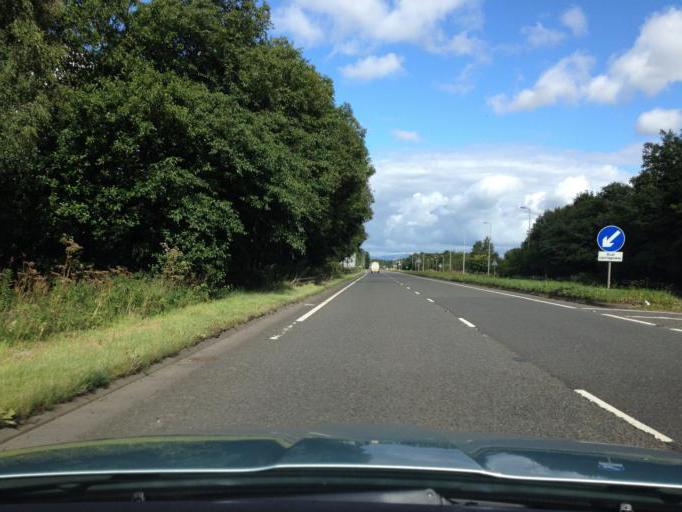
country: GB
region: Scotland
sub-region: West Lothian
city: Bathgate
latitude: 55.9160
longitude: -3.6770
